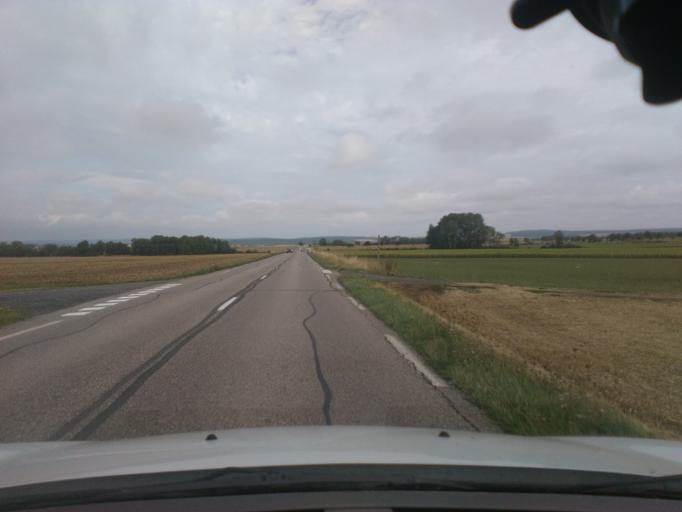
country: FR
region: Lorraine
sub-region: Departement de Meurthe-et-Moselle
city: Vezelise
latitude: 48.4835
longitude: 6.1429
